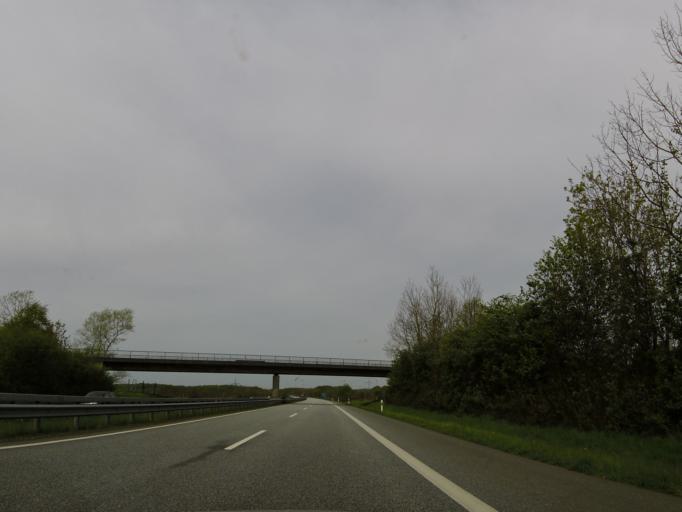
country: DE
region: Schleswig-Holstein
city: Hadenfeld
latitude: 54.0213
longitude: 9.4595
